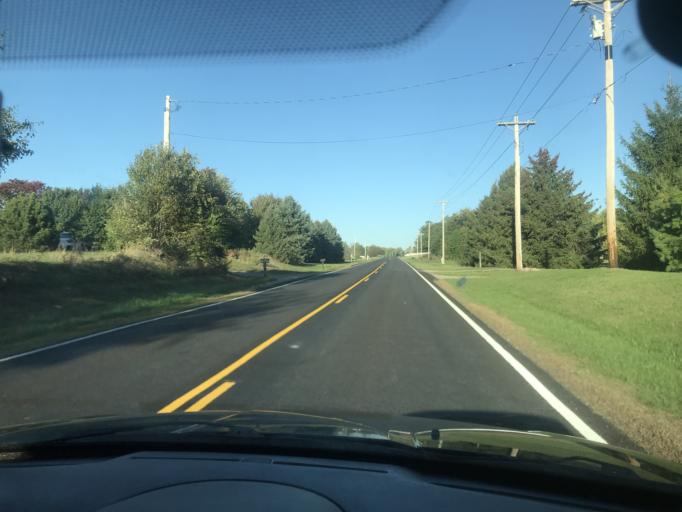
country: US
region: Ohio
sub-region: Logan County
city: Bellefontaine
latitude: 40.3219
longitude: -83.7911
